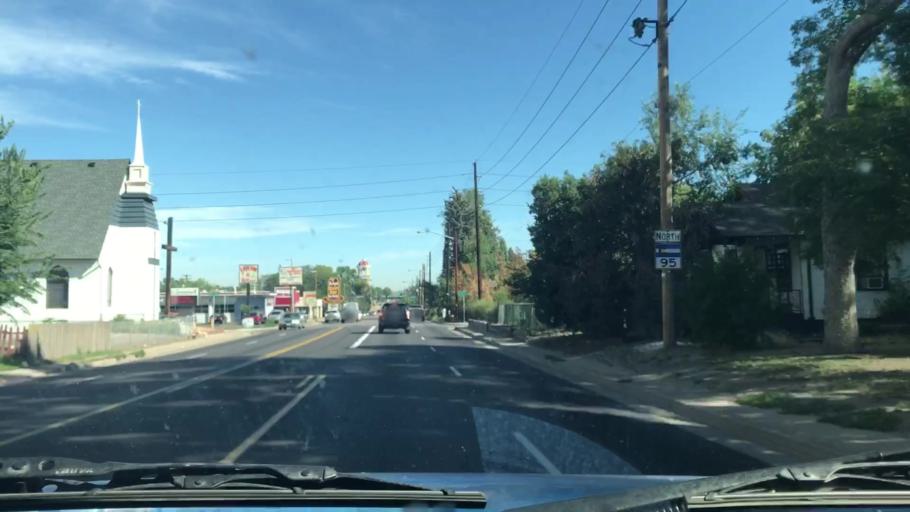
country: US
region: Colorado
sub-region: Jefferson County
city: Edgewater
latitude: 39.7741
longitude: -105.0532
